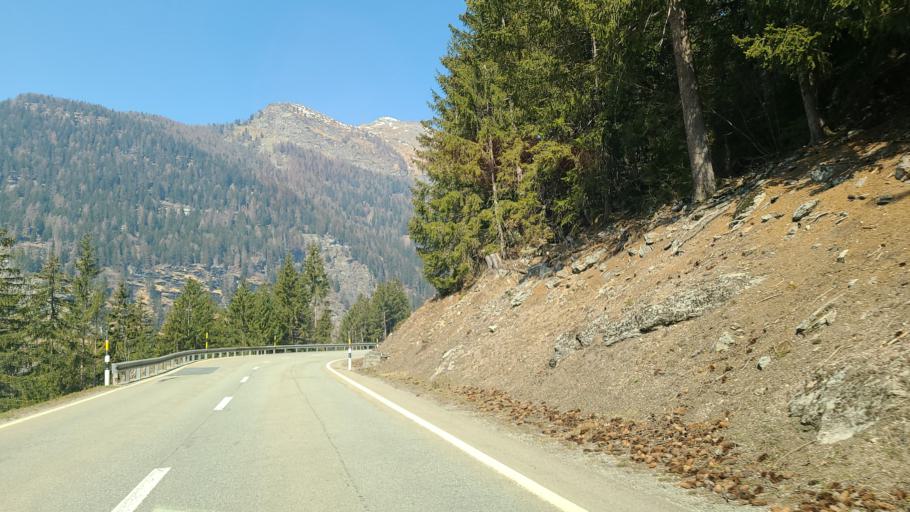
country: CH
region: Grisons
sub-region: Bernina District
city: Poschiavo
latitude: 46.3680
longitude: 10.0735
